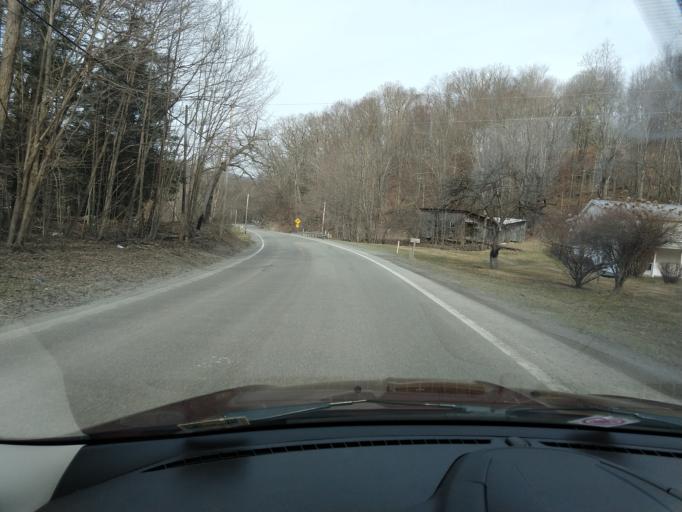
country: US
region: West Virginia
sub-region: Tucker County
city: Parsons
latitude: 38.9040
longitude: -79.4904
